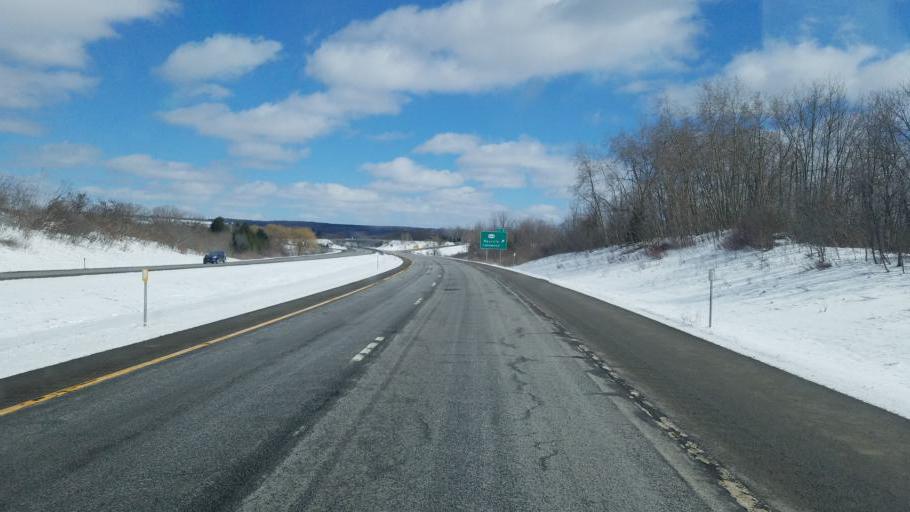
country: US
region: New York
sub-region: Chautauqua County
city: Lakewood
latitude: 42.1518
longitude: -79.4151
